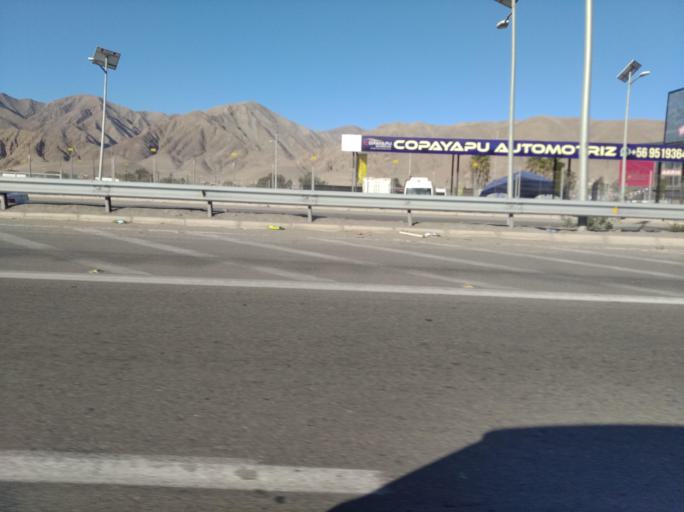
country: CL
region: Atacama
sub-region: Provincia de Copiapo
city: Copiapo
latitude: -27.3527
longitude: -70.3539
